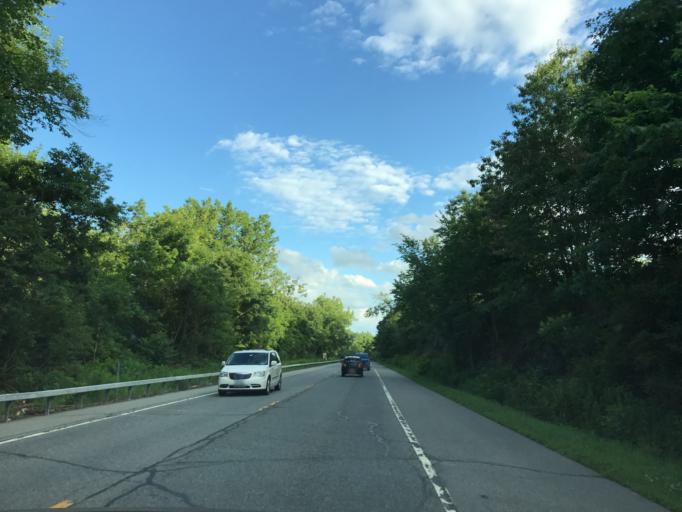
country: US
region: New York
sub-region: Saratoga County
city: Schuylerville
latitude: 43.0861
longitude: -73.5835
